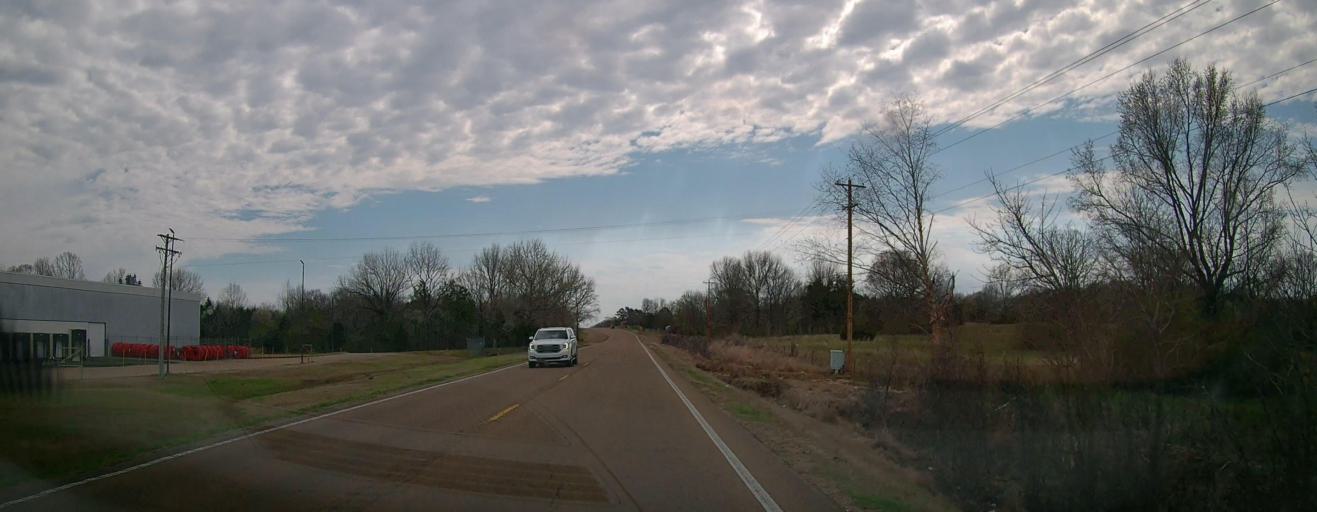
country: US
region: Mississippi
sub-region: Marshall County
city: Byhalia
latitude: 34.8640
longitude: -89.6605
